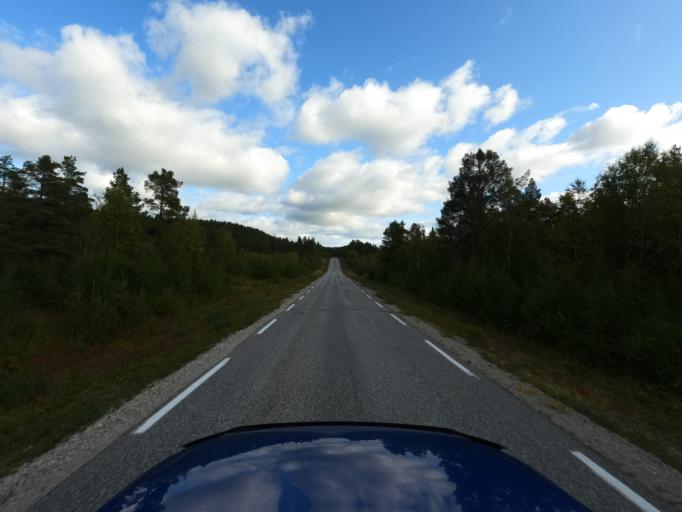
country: NO
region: Finnmark Fylke
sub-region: Karasjok
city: Karasjohka
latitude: 69.4345
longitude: 25.1531
